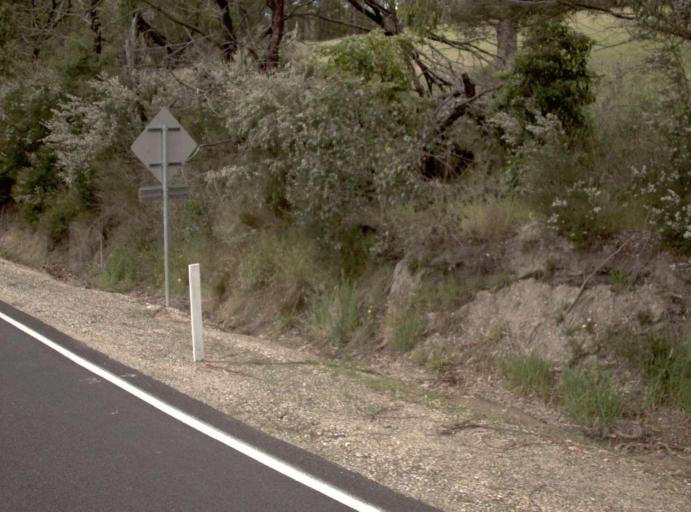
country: AU
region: New South Wales
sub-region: Bombala
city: Bombala
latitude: -37.4726
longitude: 149.1763
